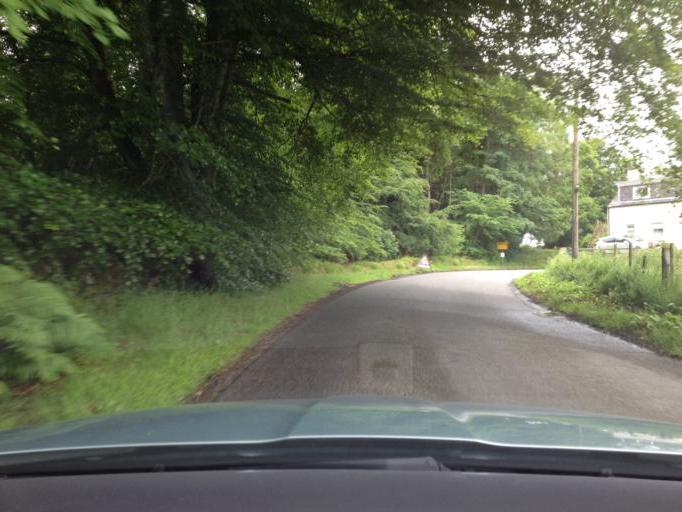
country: GB
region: Scotland
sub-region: Angus
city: Brechin
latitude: 56.8426
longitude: -2.6695
